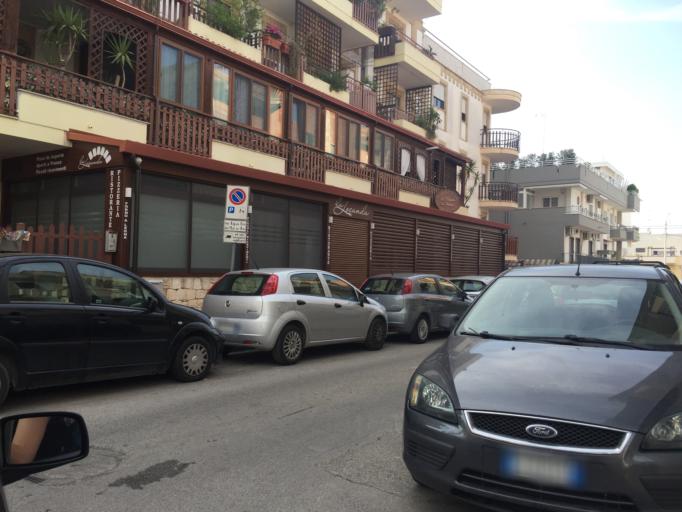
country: IT
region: Apulia
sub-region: Provincia di Bari
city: Capurso
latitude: 41.0479
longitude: 16.9172
